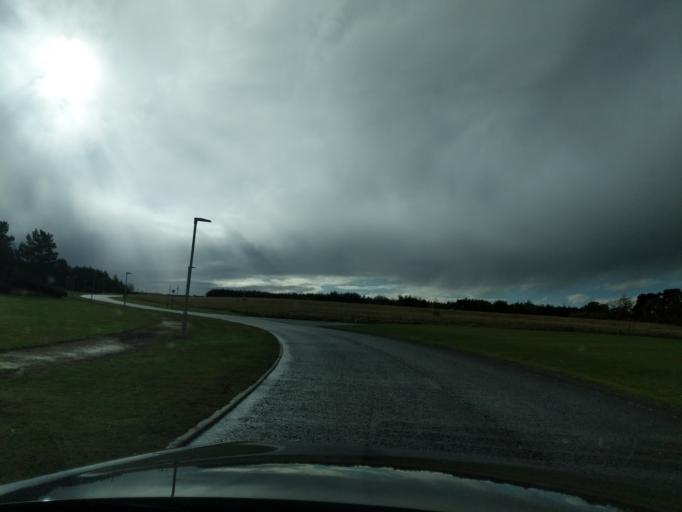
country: GB
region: Scotland
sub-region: Fife
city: Saint Andrews
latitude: 56.3210
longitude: -2.7372
